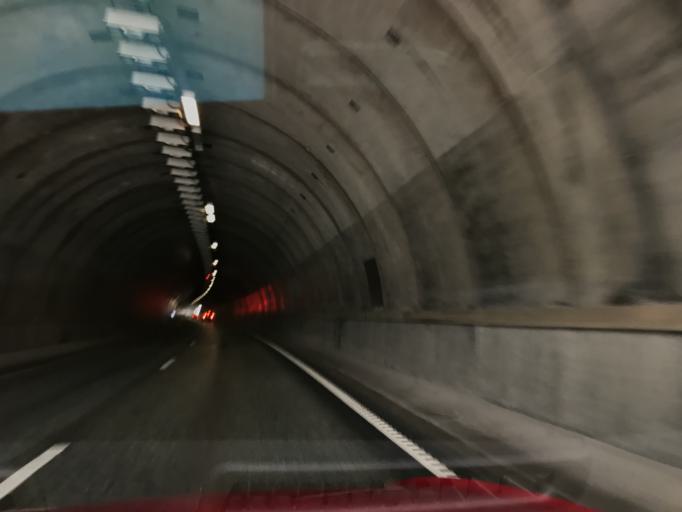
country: NO
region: Vest-Agder
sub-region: Kristiansand
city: Justvik
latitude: 58.1615
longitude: 8.0686
